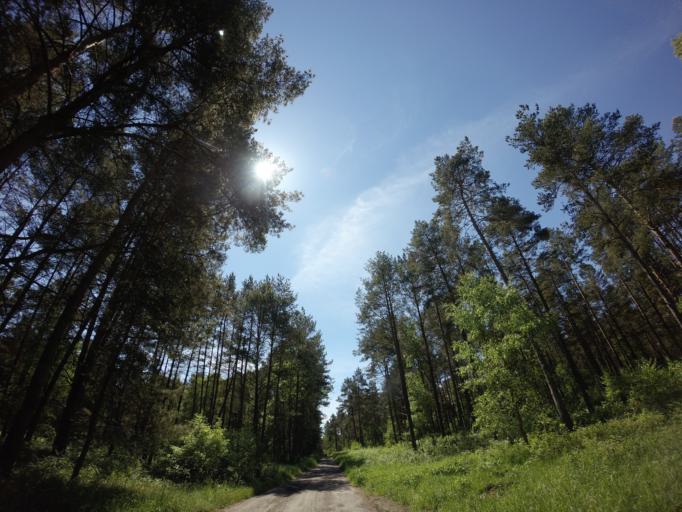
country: PL
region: West Pomeranian Voivodeship
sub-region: Powiat choszczenski
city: Drawno
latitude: 53.3047
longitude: 15.6912
